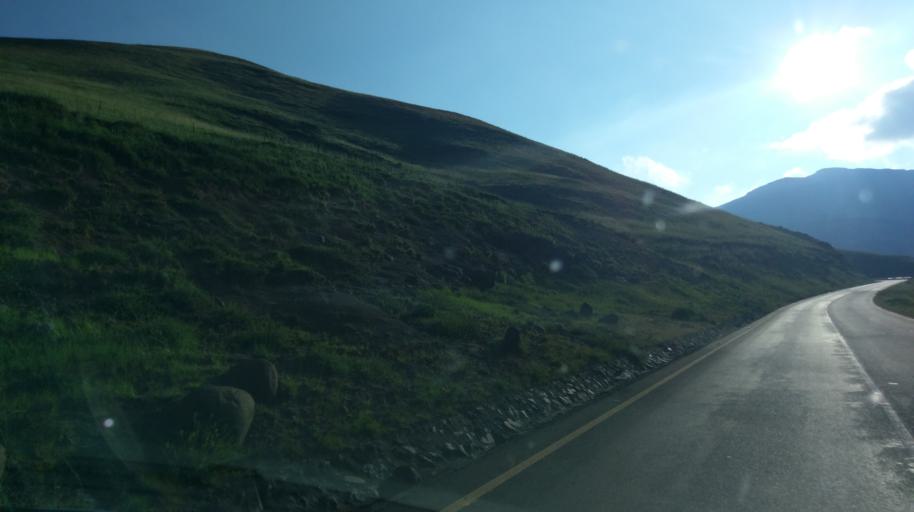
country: LS
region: Butha-Buthe
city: Butha-Buthe
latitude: -29.1108
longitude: 28.4606
